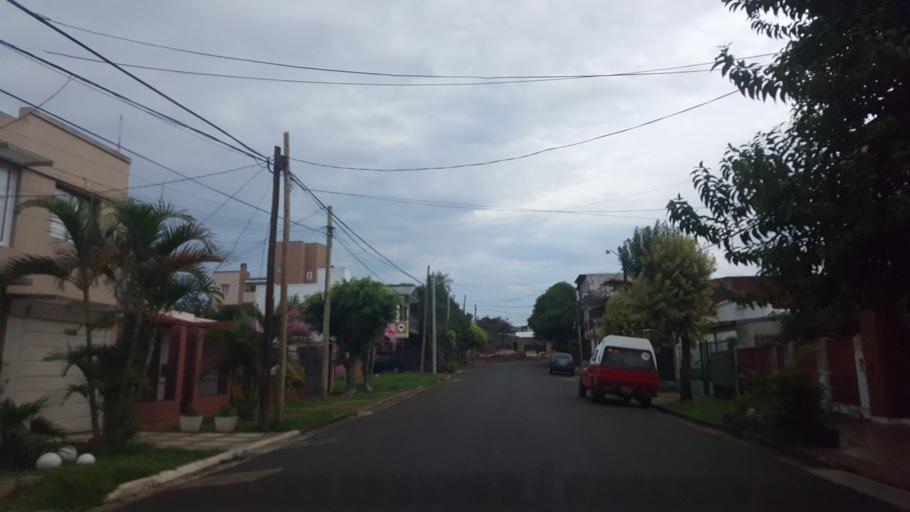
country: AR
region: Misiones
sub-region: Departamento de Capital
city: Posadas
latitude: -27.3820
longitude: -55.8968
